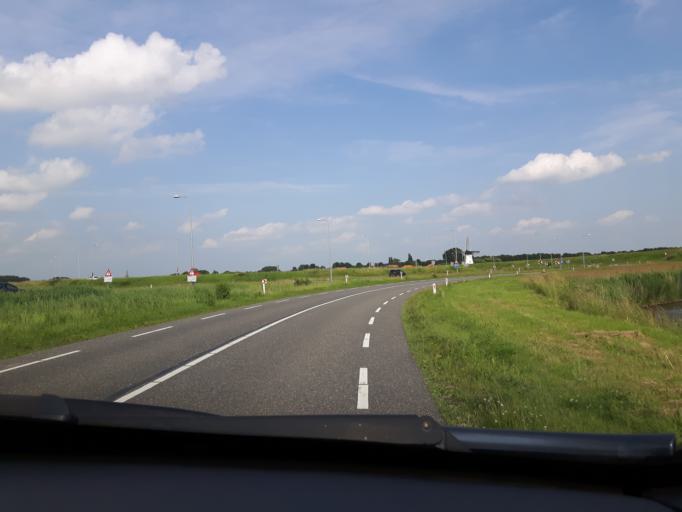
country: NL
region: Zeeland
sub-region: Gemeente Middelburg
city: Middelburg
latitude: 51.4793
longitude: 3.6479
